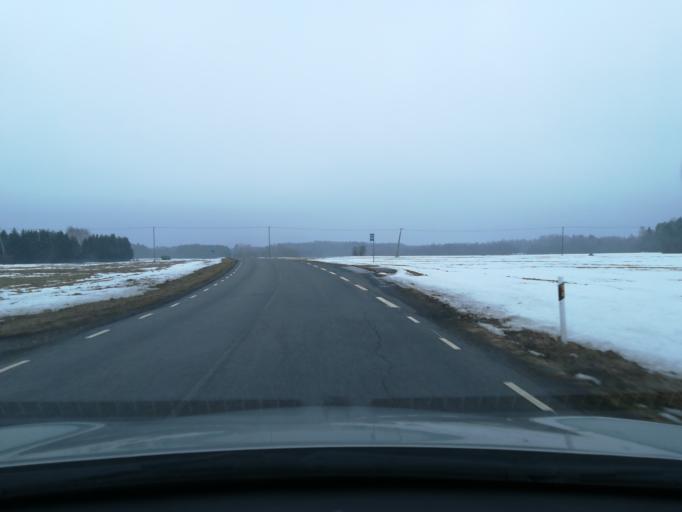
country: EE
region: Harju
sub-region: Kuusalu vald
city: Kuusalu
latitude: 59.4725
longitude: 25.5881
